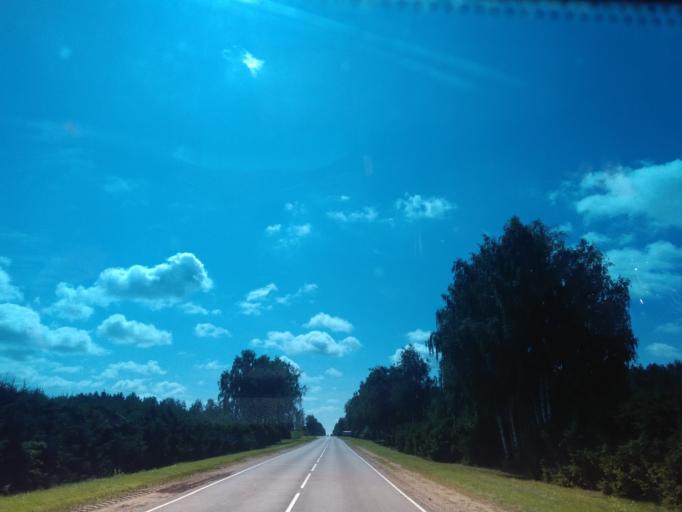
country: BY
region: Minsk
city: Uzda
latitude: 53.3564
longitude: 27.2250
